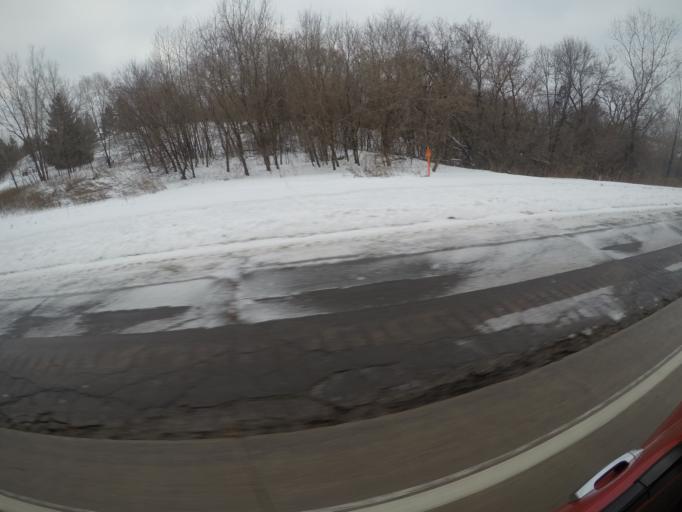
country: US
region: Minnesota
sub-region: Dakota County
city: Inver Grove Heights
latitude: 44.8326
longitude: -93.0790
